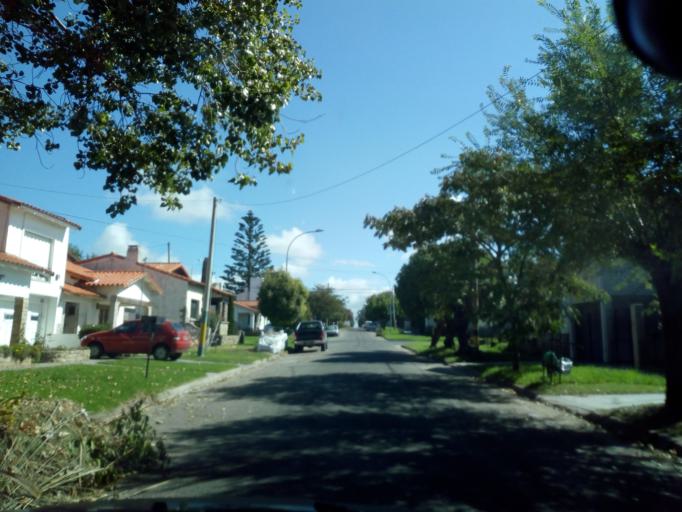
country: AR
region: Buenos Aires
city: Mar del Plata
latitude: -38.0662
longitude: -57.5503
